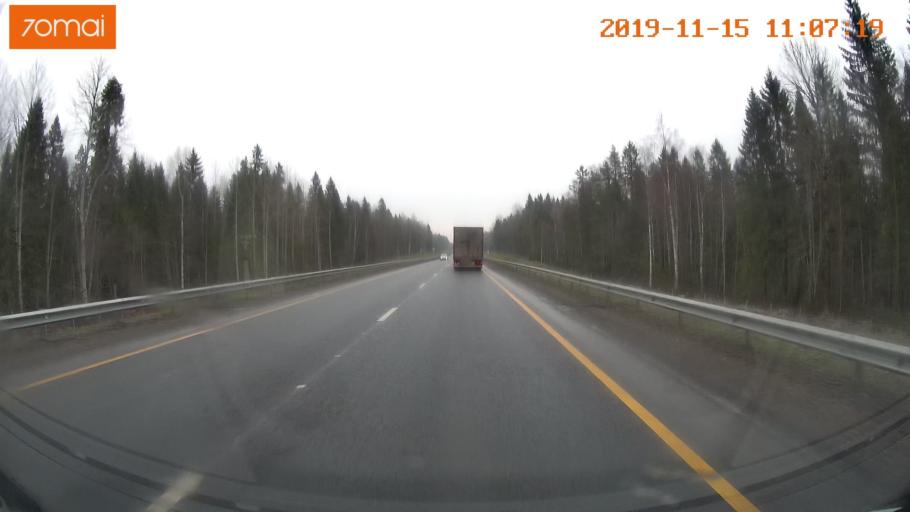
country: RU
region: Vologda
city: Chebsara
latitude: 59.1194
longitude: 39.0476
